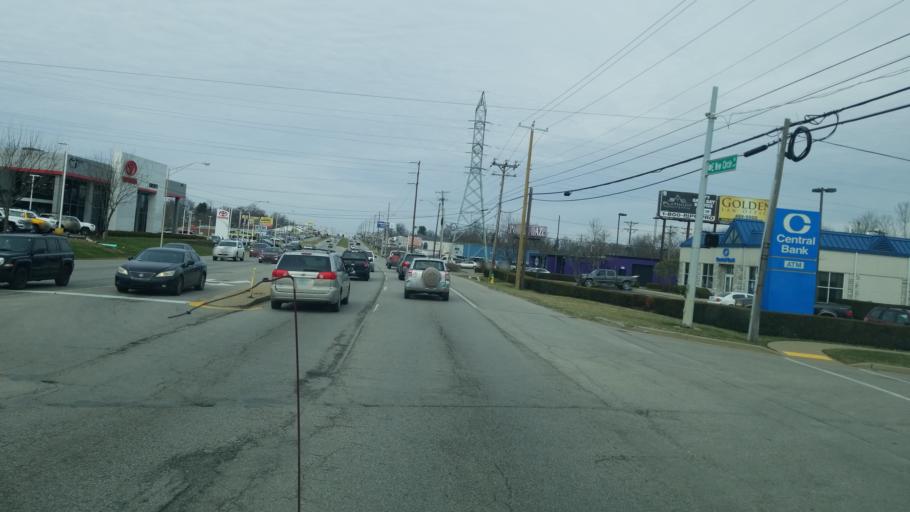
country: US
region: Kentucky
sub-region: Fayette County
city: Lexington-Fayette
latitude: 38.0498
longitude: -84.4550
